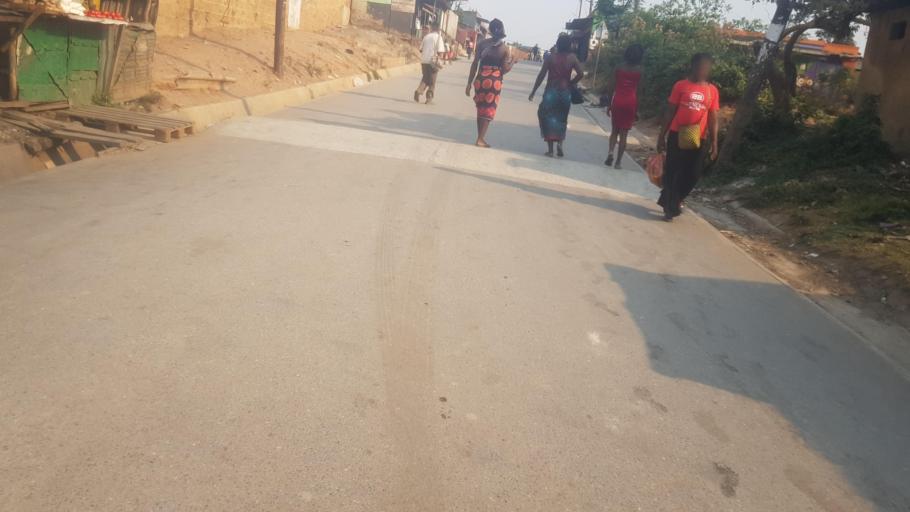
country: ZM
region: Lusaka
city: Lusaka
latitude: -15.4420
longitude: 28.3845
